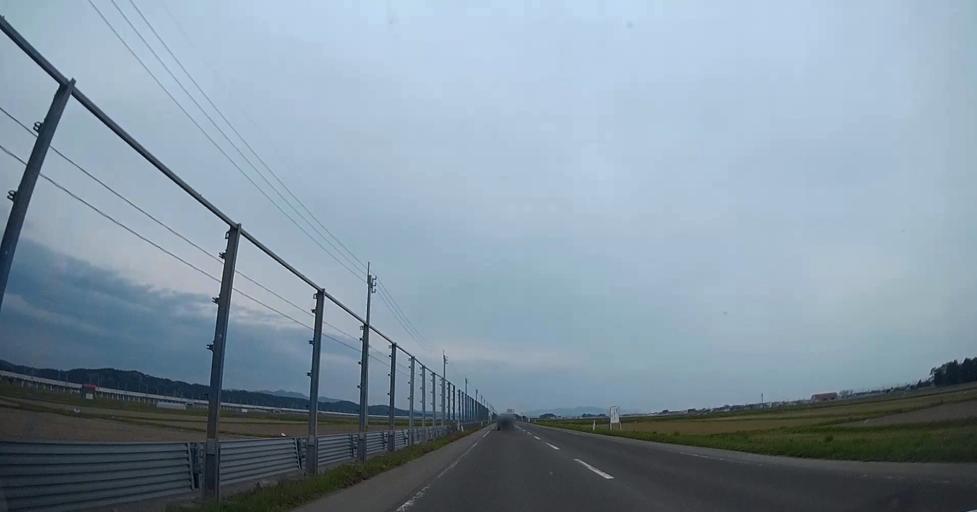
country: JP
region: Aomori
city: Aomori Shi
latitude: 40.8709
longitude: 140.6750
